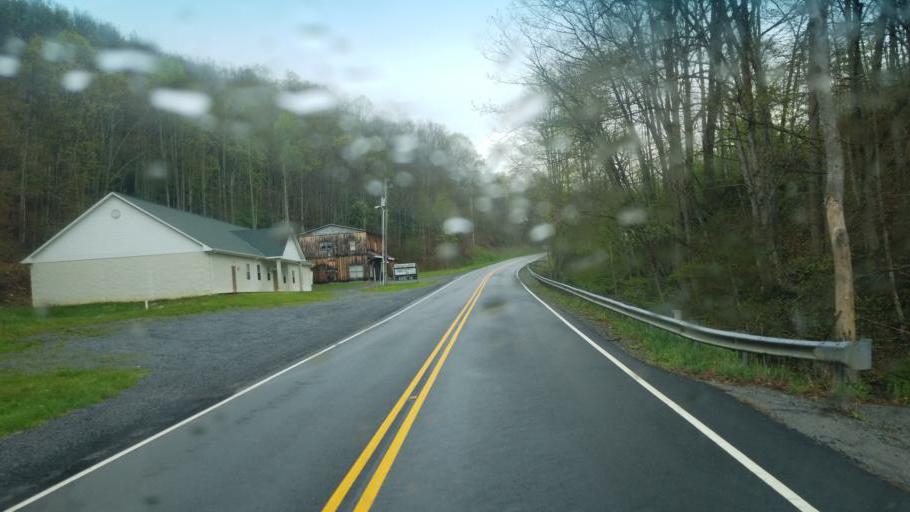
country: US
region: Virginia
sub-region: Smyth County
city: Marion
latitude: 36.8126
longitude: -81.4597
